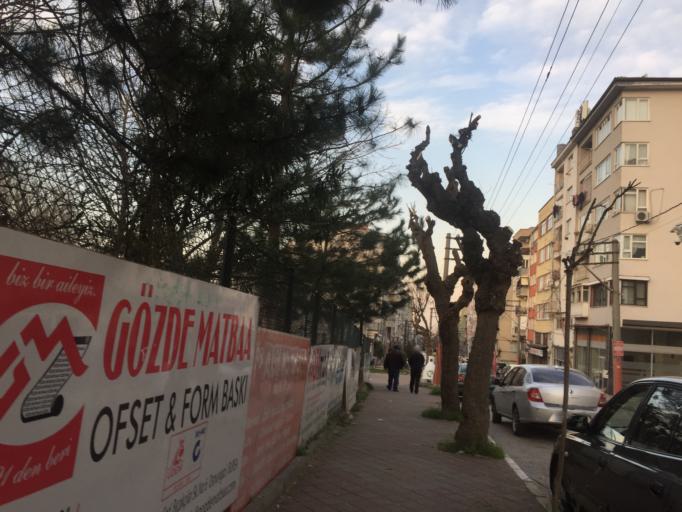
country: TR
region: Bursa
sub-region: Osmangazi
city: Bursa
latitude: 40.1850
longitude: 29.0757
